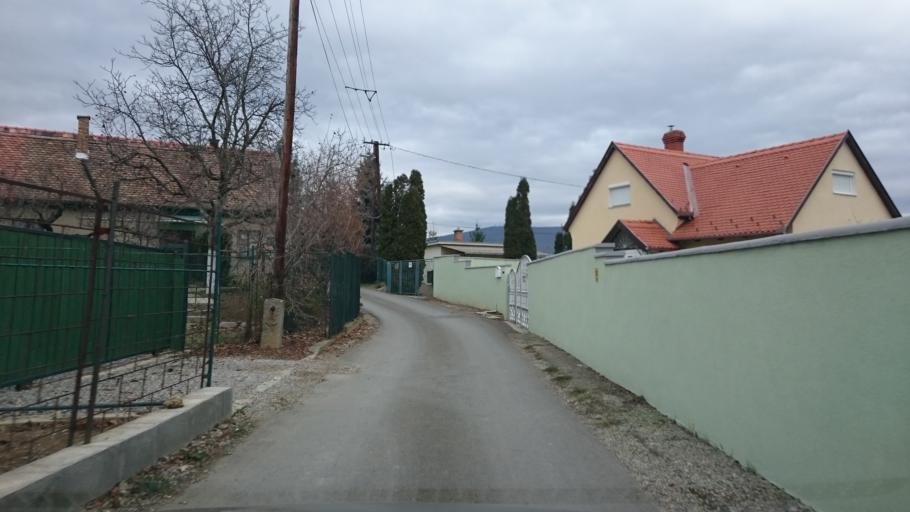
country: HU
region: Baranya
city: Pellerd
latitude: 46.0728
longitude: 18.1811
